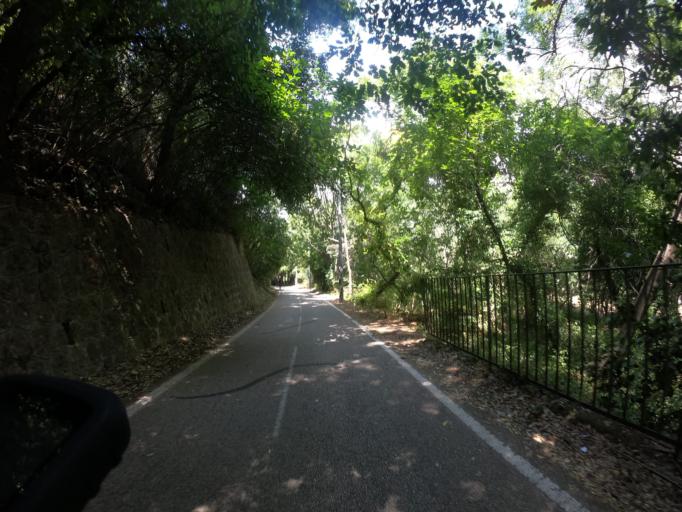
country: FR
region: Provence-Alpes-Cote d'Azur
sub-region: Departement du Var
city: La Valette-du-Var
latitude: 43.1230
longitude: 5.9621
